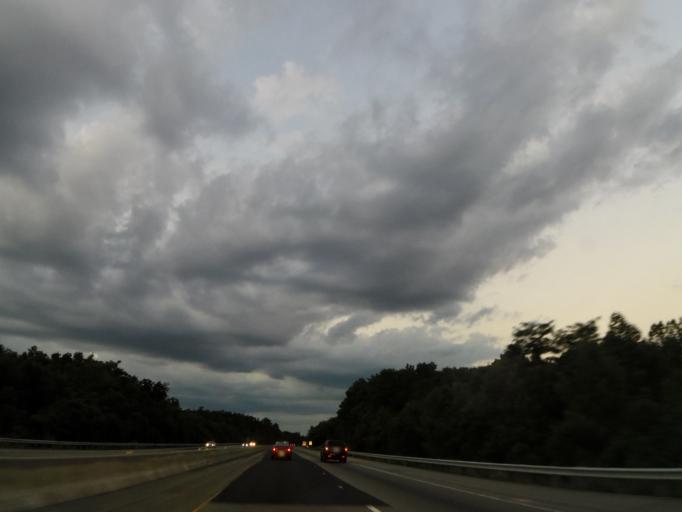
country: US
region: Tennessee
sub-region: Putnam County
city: Monterey
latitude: 36.1332
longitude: -85.3404
